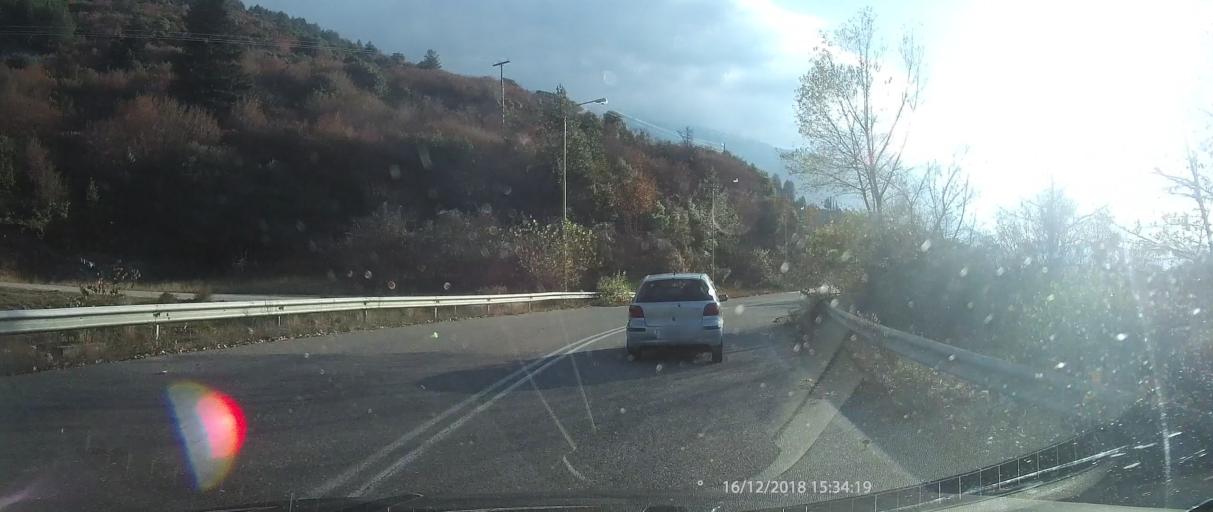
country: GR
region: Epirus
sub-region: Nomos Ioanninon
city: Konitsa
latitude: 40.0631
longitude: 20.7429
